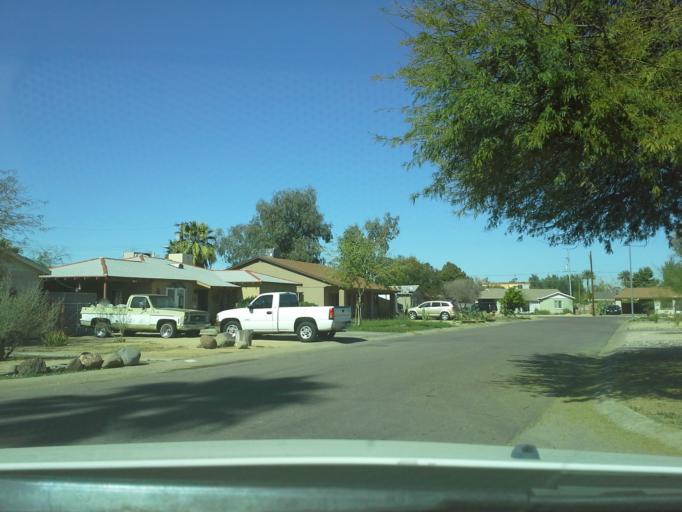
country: US
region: Arizona
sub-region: Maricopa County
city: Phoenix
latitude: 33.4973
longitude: -112.0586
